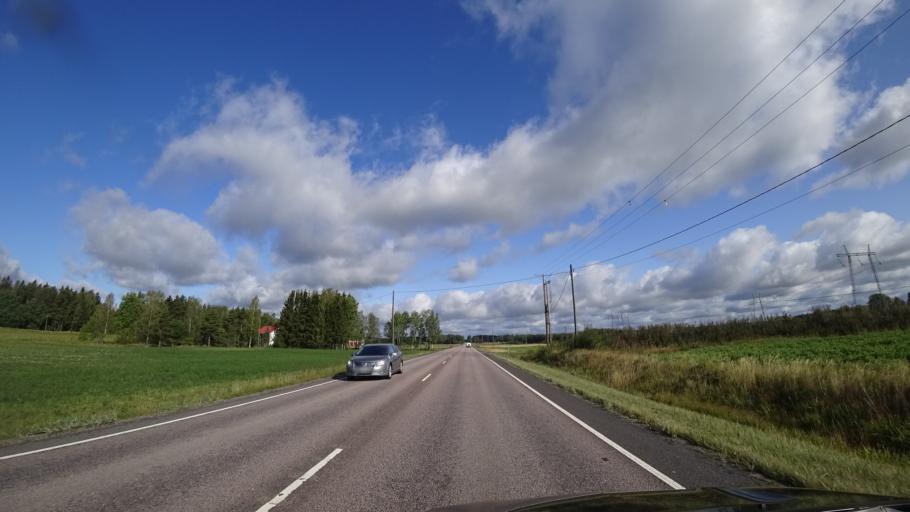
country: FI
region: Uusimaa
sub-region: Helsinki
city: Nurmijaervi
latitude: 60.5143
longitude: 24.9271
